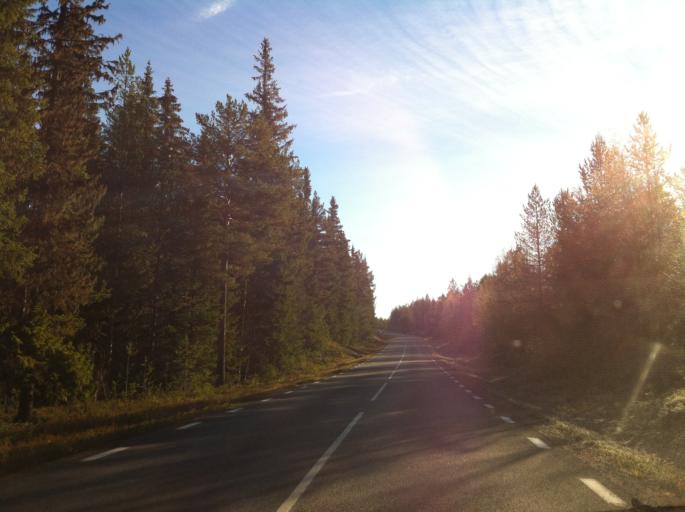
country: NO
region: Hedmark
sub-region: Engerdal
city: Engerdal
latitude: 61.9913
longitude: 12.4606
